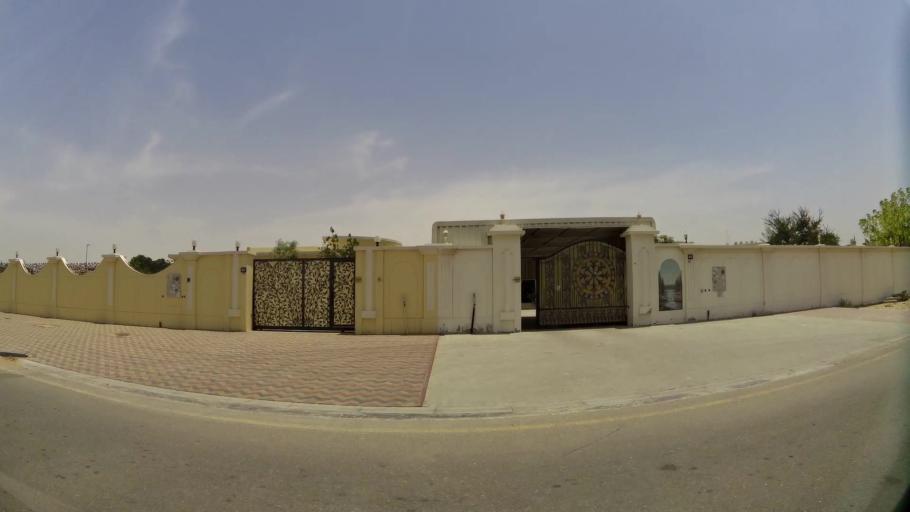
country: AE
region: Ash Shariqah
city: Sharjah
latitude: 25.2462
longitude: 55.4668
